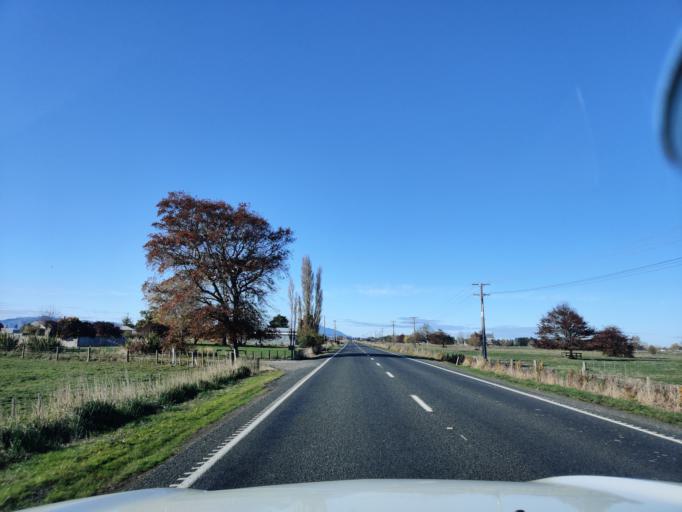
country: NZ
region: Waikato
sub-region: Hauraki District
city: Ngatea
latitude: -37.2868
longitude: 175.5472
